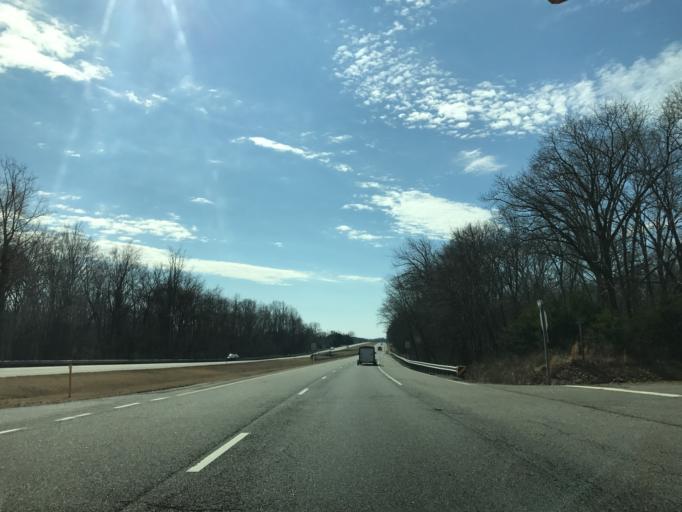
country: US
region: Maryland
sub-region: Queen Anne's County
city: Kingstown
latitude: 39.2571
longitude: -75.8653
